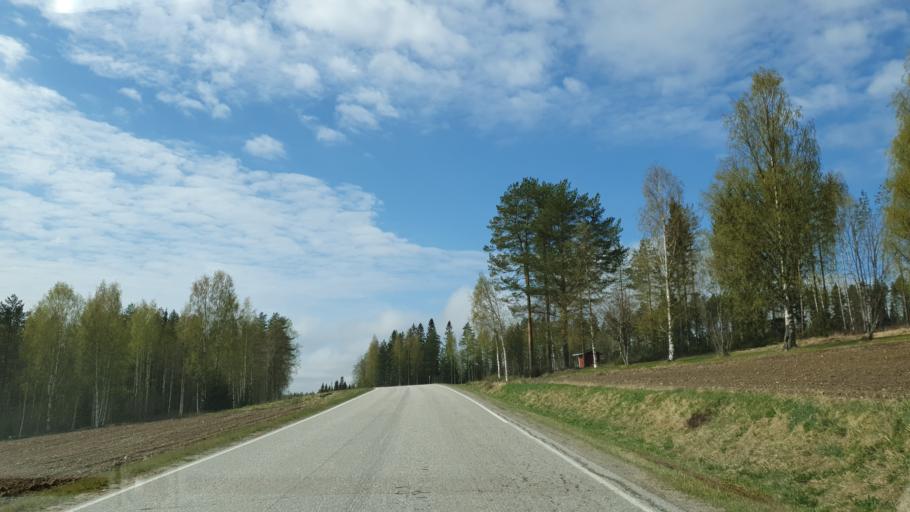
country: FI
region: Kainuu
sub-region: Kehys-Kainuu
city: Kuhmo
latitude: 64.1251
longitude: 29.6465
